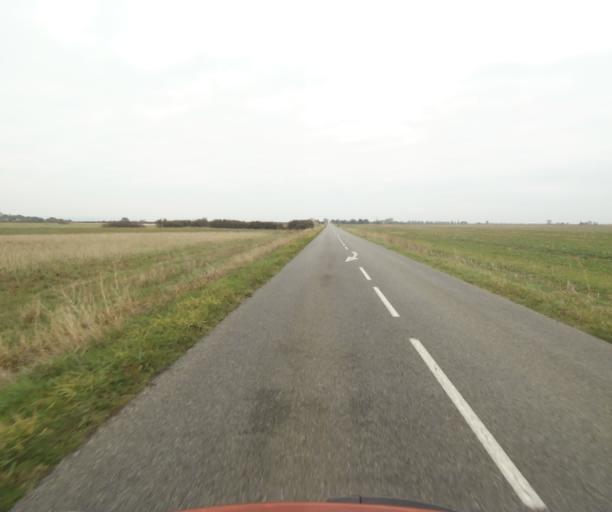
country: FR
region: Midi-Pyrenees
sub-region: Departement du Tarn-et-Garonne
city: Verdun-sur-Garonne
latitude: 43.8161
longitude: 1.1916
